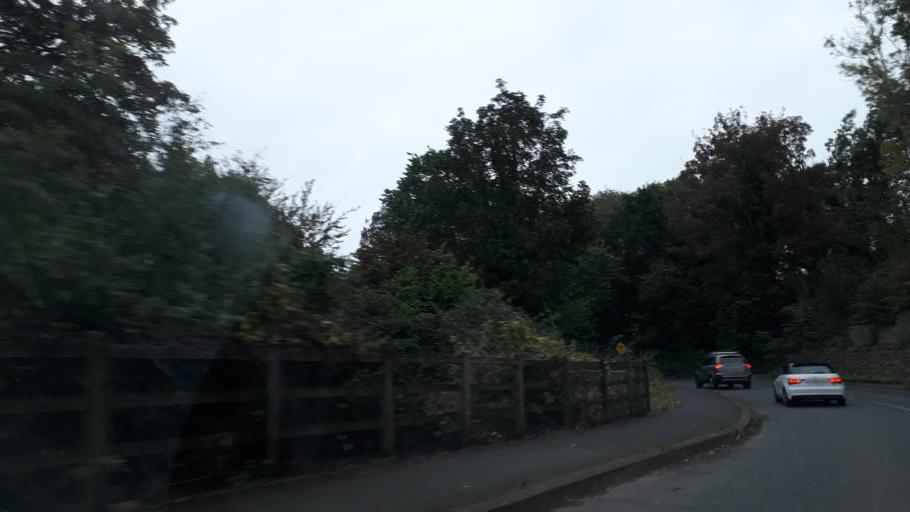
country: IE
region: Leinster
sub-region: Wicklow
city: Enniskerry
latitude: 53.1898
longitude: -6.1520
